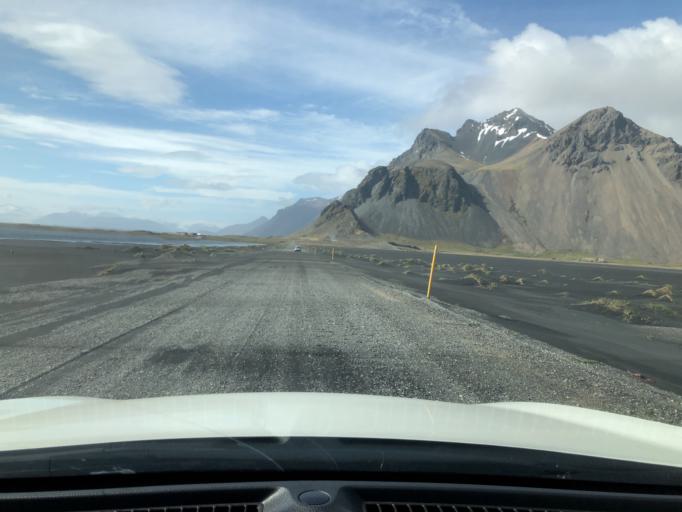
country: IS
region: East
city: Hoefn
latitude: 64.2464
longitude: -14.9762
